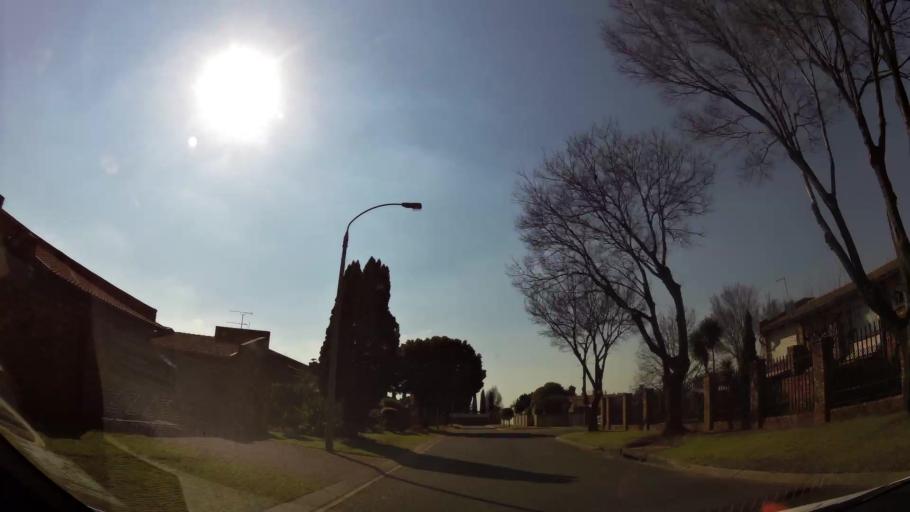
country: ZA
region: Gauteng
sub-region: Ekurhuleni Metropolitan Municipality
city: Boksburg
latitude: -26.1814
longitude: 28.2791
